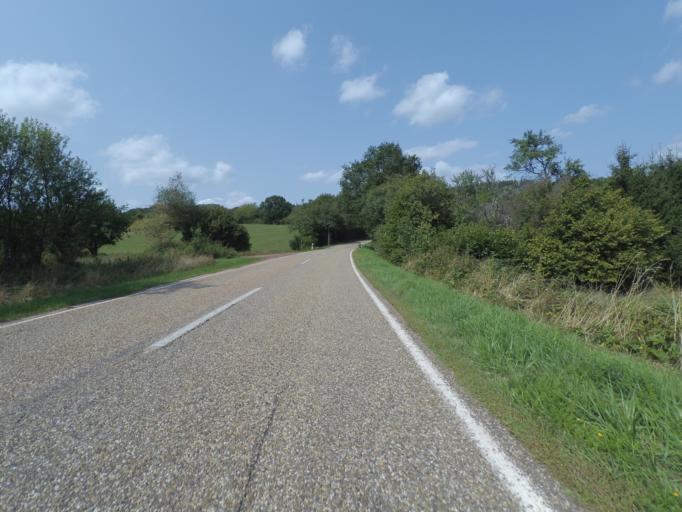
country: DE
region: Saarland
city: Britten
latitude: 49.5173
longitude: 6.6821
